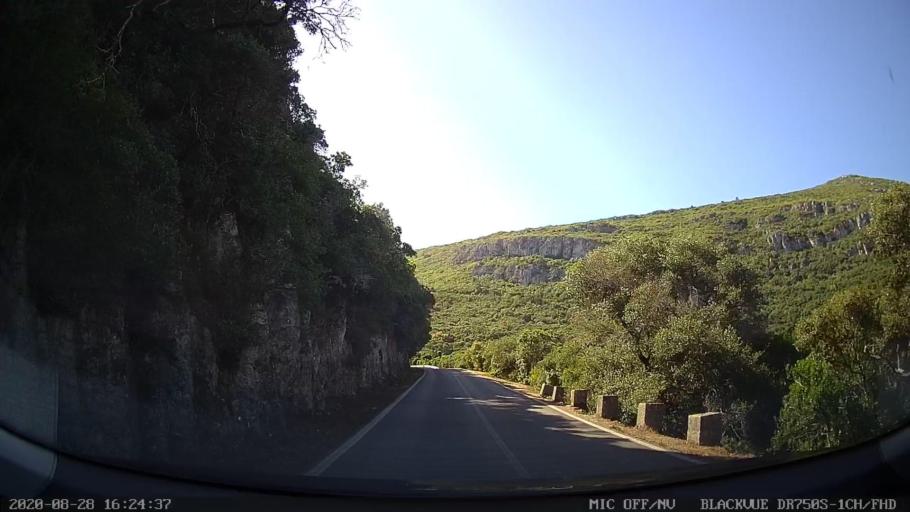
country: PT
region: Setubal
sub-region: Sesimbra
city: Sesimbra
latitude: 38.4696
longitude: -9.0007
